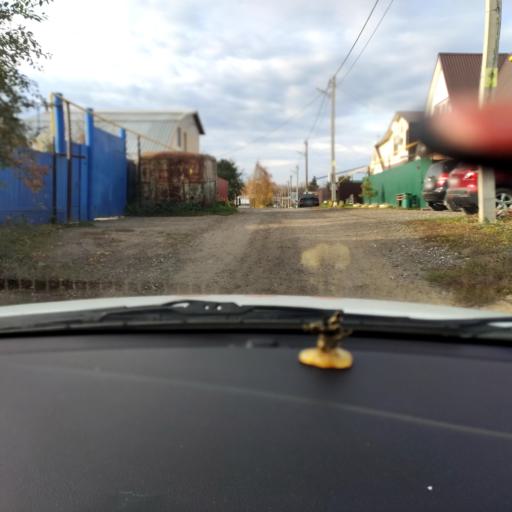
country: RU
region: Tatarstan
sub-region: Gorod Kazan'
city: Kazan
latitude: 55.7369
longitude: 49.0965
